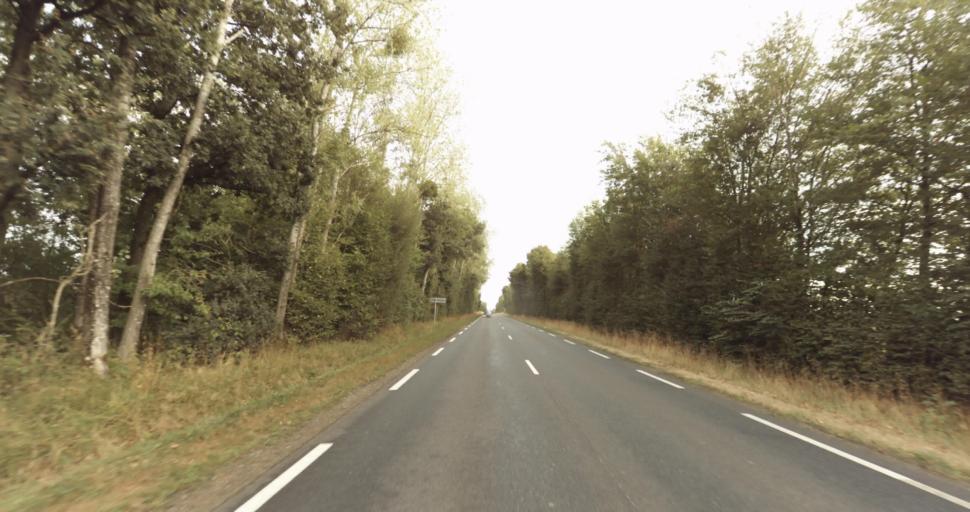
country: FR
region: Lower Normandy
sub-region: Departement de l'Orne
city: Vimoutiers
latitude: 48.8825
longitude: 0.2559
